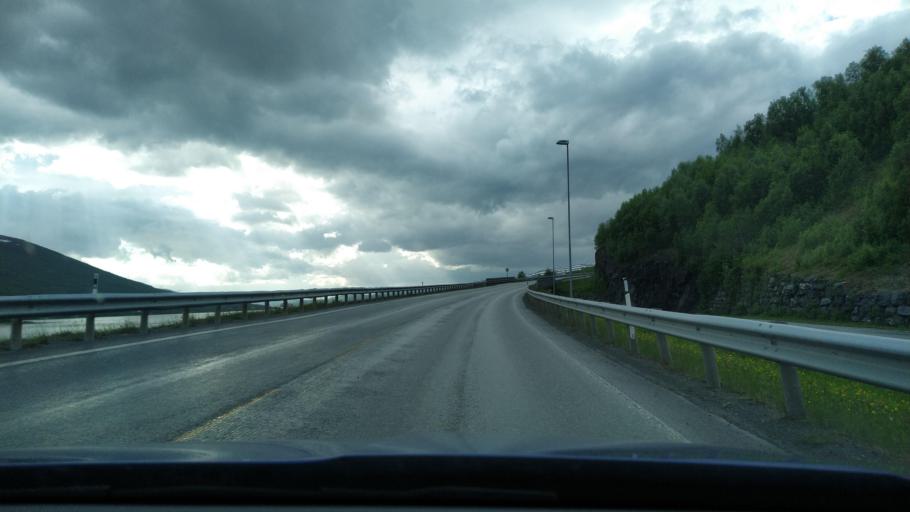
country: NO
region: Troms
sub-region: Balsfjord
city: Storsteinnes
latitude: 69.2229
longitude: 19.5114
